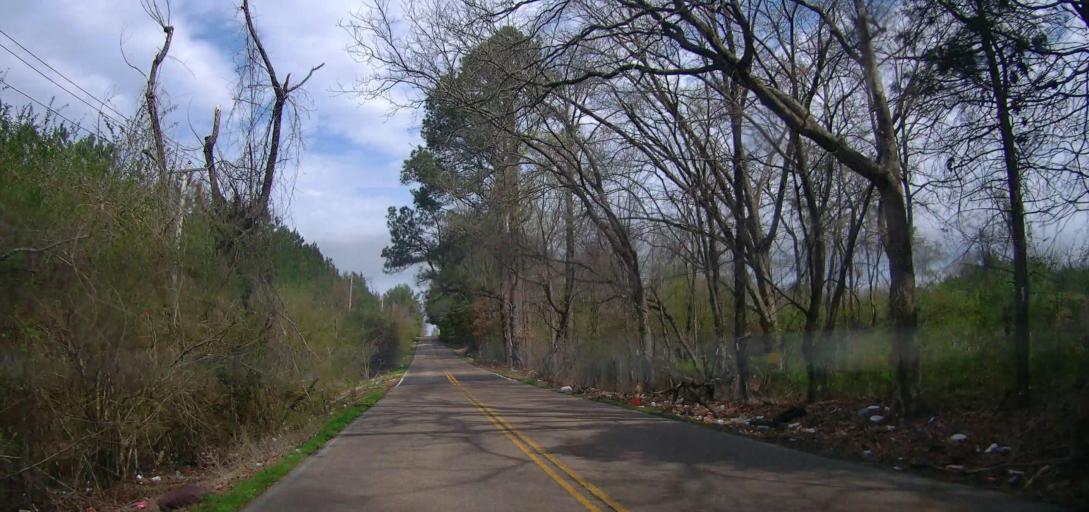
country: US
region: Mississippi
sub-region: De Soto County
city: Olive Branch
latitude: 34.9962
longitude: -89.8484
